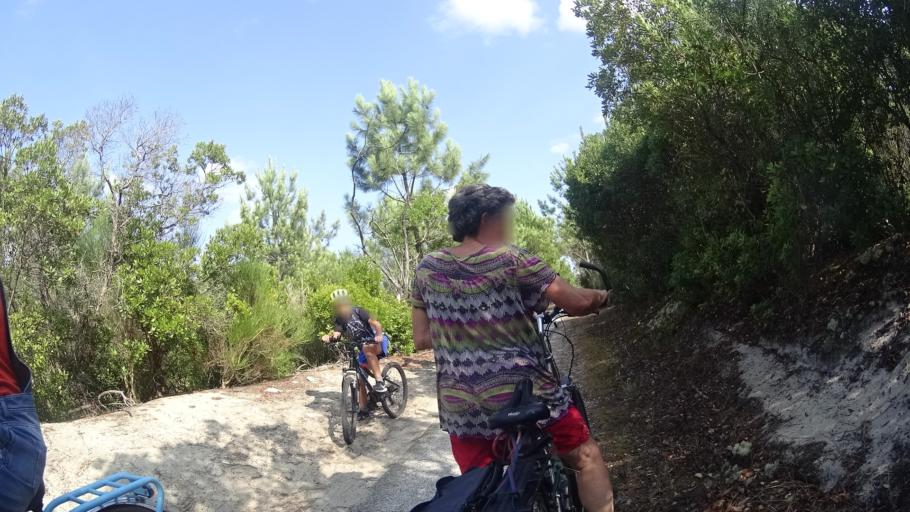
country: FR
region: Aquitaine
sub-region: Departement de la Gironde
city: Lacanau
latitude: 44.9666
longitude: -1.1795
